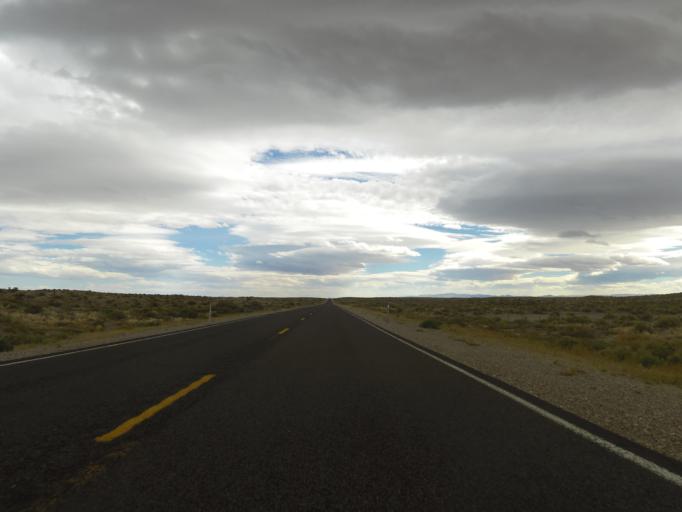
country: US
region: Nevada
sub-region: Churchill County
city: Fallon
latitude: 39.5989
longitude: -118.7816
